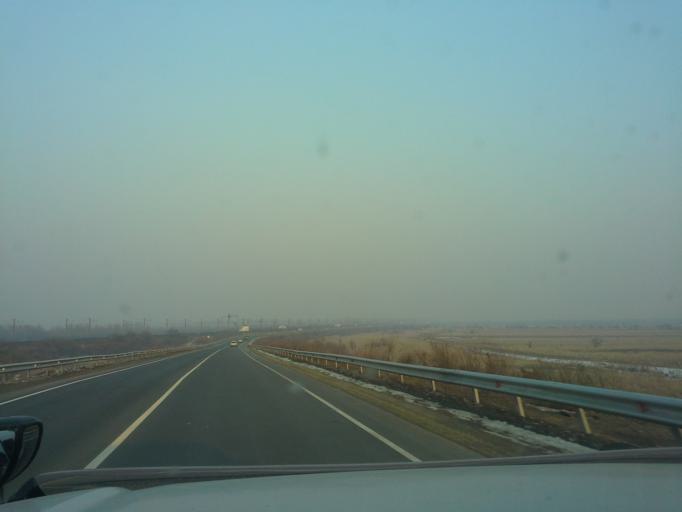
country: RU
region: Jewish Autonomous Oblast
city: Priamurskiy
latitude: 48.5232
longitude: 134.9193
